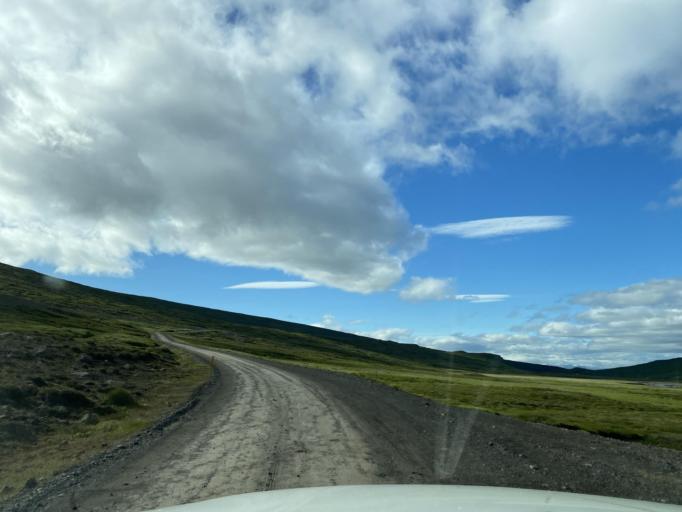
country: IS
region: East
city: Egilsstadir
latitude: 65.1877
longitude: -14.3305
